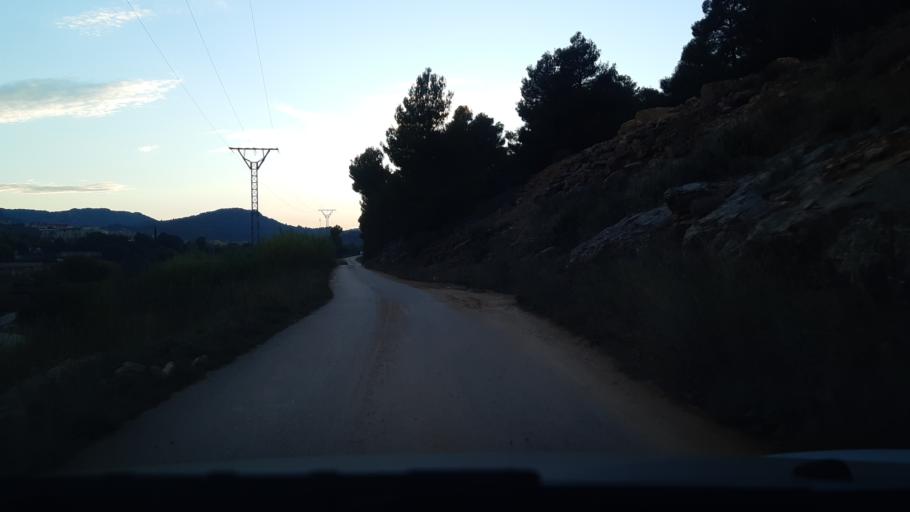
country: ES
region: Aragon
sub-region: Provincia de Teruel
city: Valderrobres
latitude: 40.8411
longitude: 0.1949
